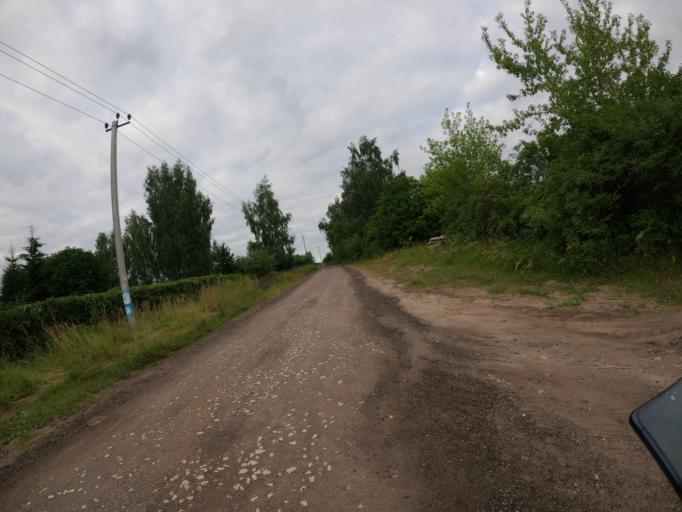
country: RU
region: Moskovskaya
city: Sychevo
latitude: 54.9092
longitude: 38.7349
